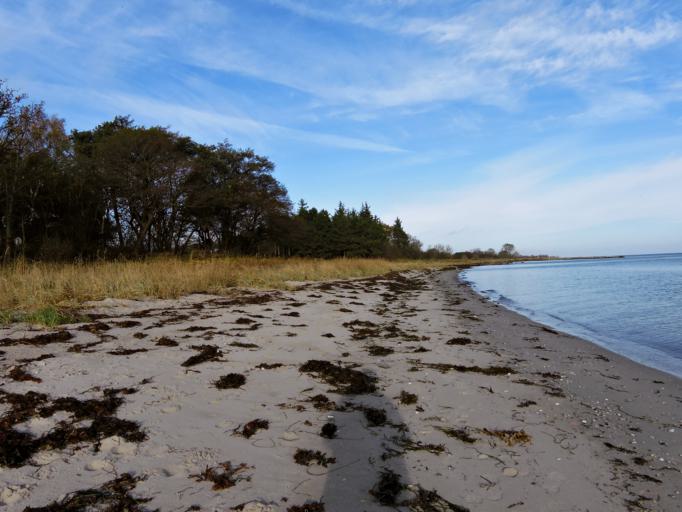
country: DK
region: Central Jutland
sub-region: Odder Kommune
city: Odder
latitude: 55.9220
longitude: 10.2568
